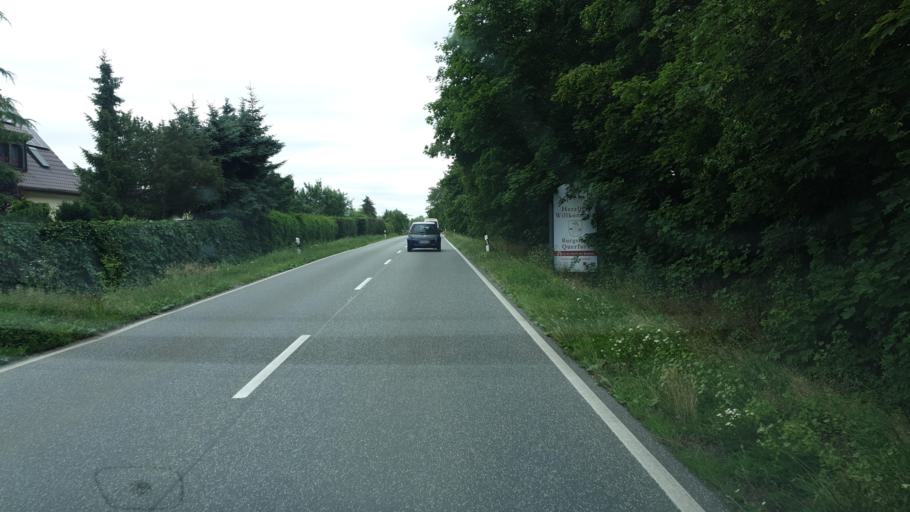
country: DE
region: Saxony-Anhalt
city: Querfurt
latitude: 51.3875
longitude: 11.5921
